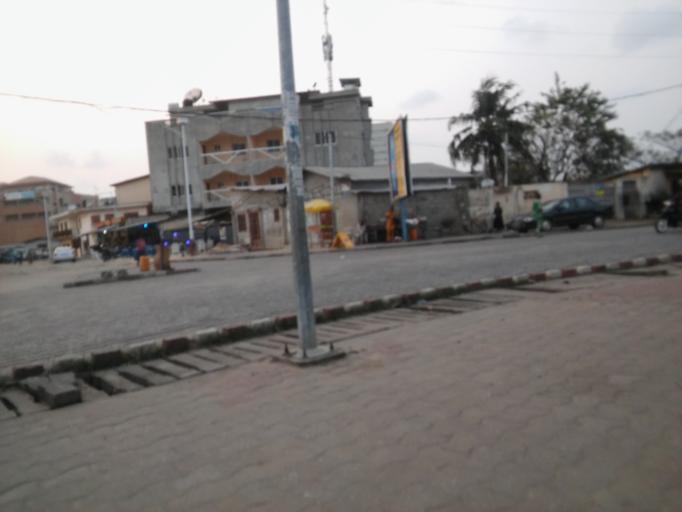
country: BJ
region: Littoral
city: Cotonou
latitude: 6.3700
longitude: 2.4463
